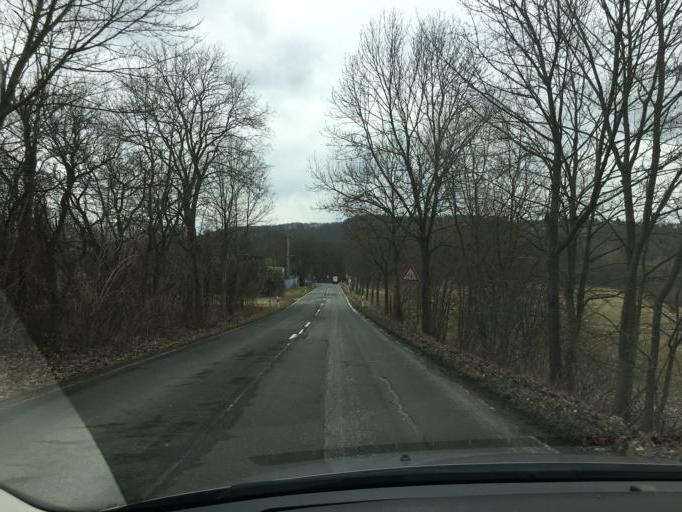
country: DE
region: Thuringia
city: Hetschburg
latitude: 50.9063
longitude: 11.2930
